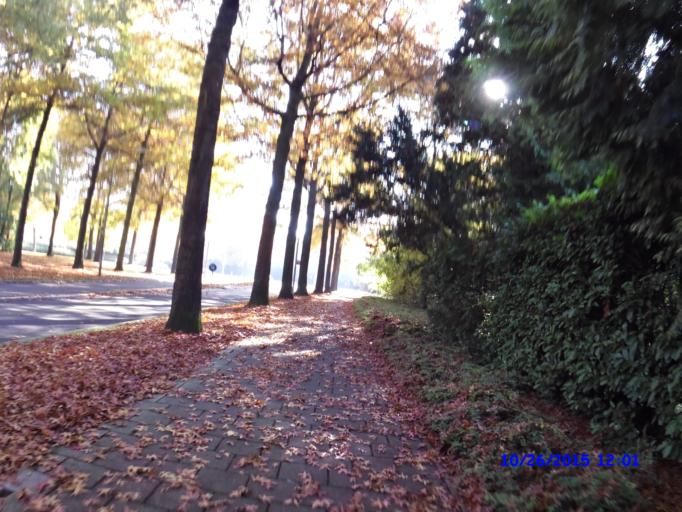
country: NL
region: North Brabant
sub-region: Gemeente Geldrop-Mierlo
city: Mierlo
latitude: 51.4380
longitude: 5.6090
